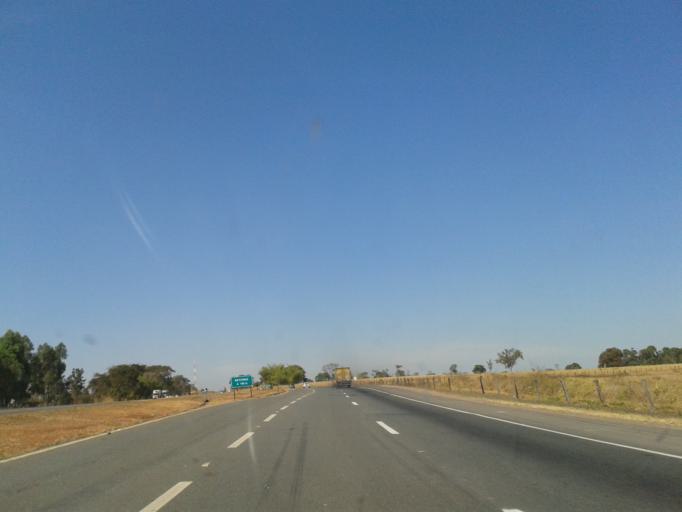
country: BR
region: Goias
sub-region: Piracanjuba
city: Piracanjuba
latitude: -17.2828
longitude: -49.2362
